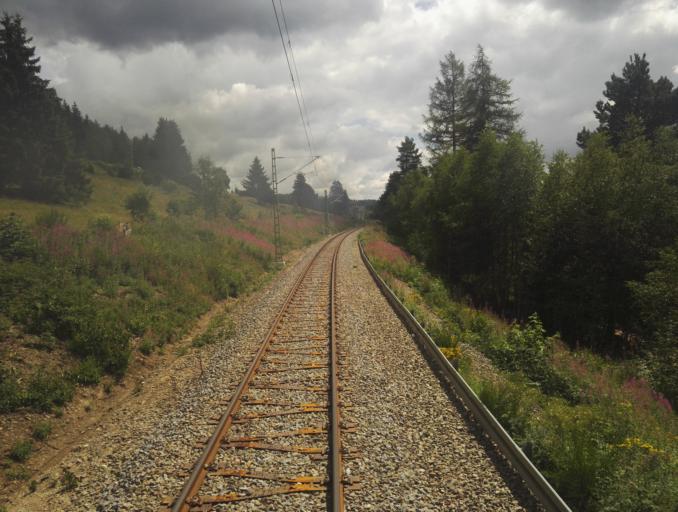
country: DE
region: Baden-Wuerttemberg
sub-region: Freiburg Region
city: Schluchsee
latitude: 47.8244
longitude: 8.1516
